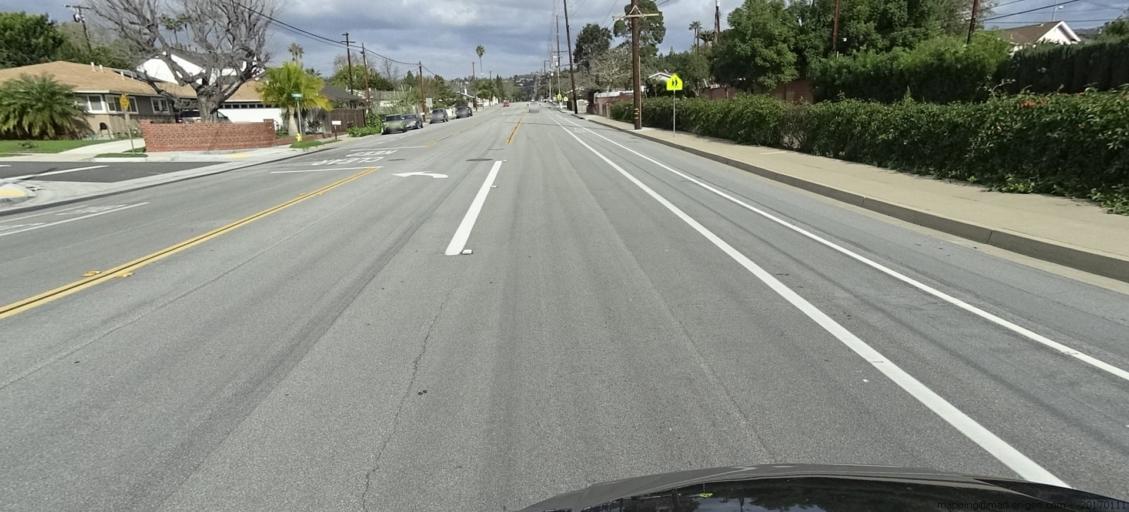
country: US
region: California
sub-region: Orange County
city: North Tustin
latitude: 33.7462
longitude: -117.8028
